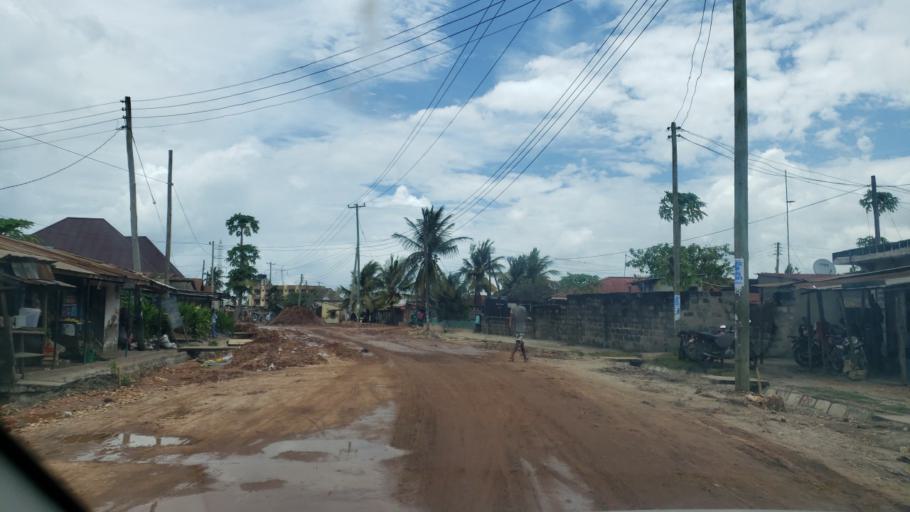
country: TZ
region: Dar es Salaam
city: Magomeni
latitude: -6.8076
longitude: 39.2337
